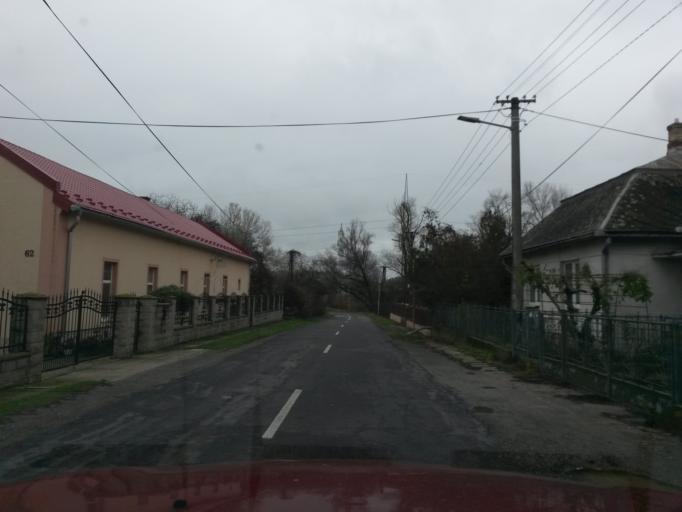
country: SK
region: Kosicky
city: Cierna nad Tisou
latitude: 48.5526
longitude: 21.9570
